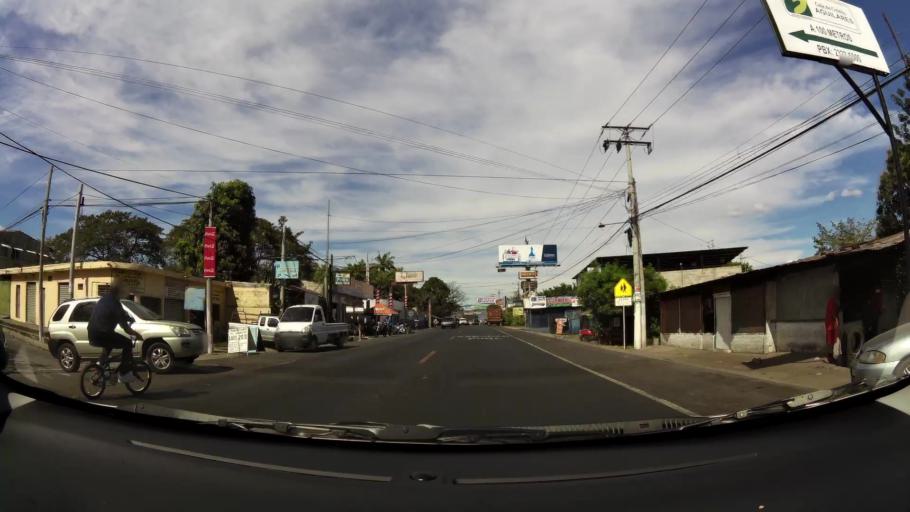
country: SV
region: San Salvador
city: Aguilares
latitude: 13.9553
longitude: -89.1854
